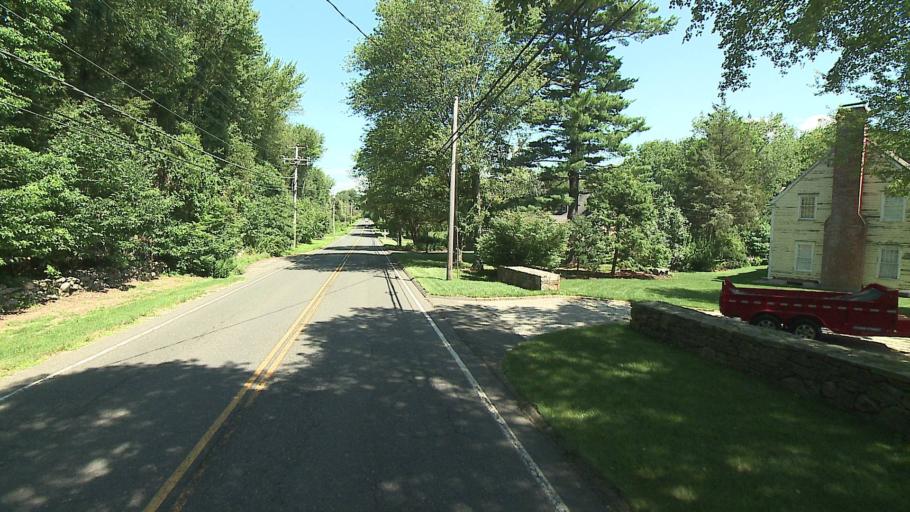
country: US
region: Connecticut
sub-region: Fairfield County
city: Trumbull
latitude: 41.3359
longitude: -73.2055
